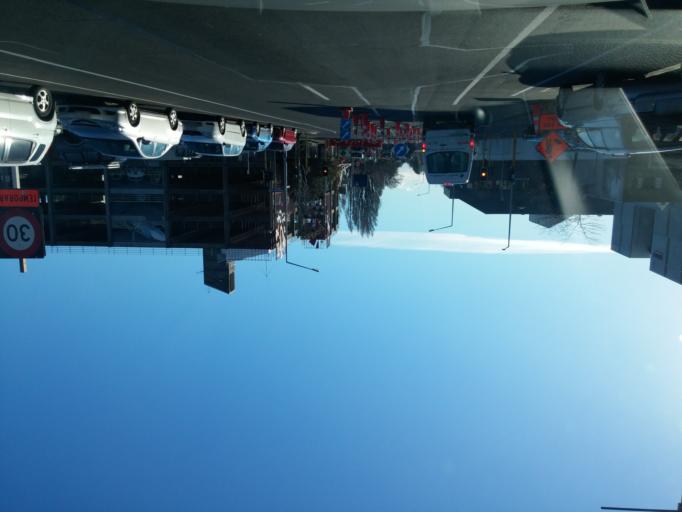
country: NZ
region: Canterbury
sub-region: Christchurch City
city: Christchurch
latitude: -43.5303
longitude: 172.6395
